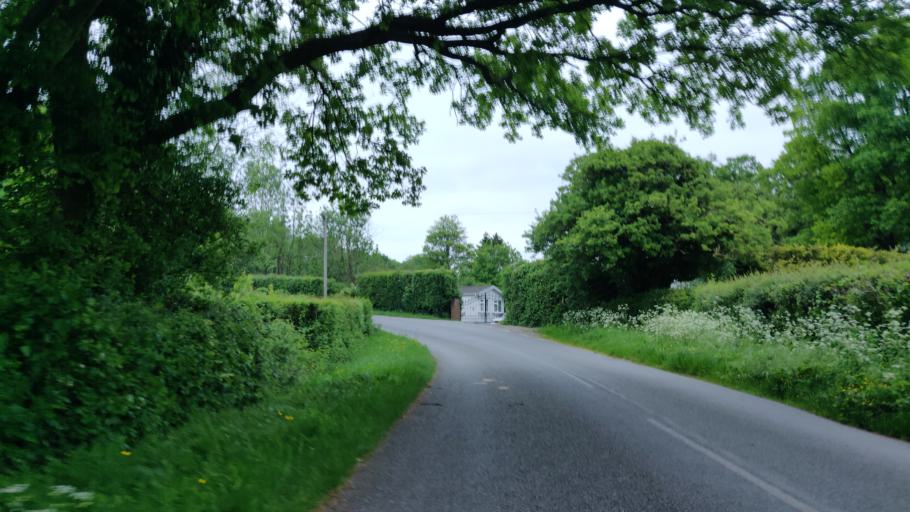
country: GB
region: England
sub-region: West Sussex
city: Southwater
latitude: 51.0316
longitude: -0.3657
